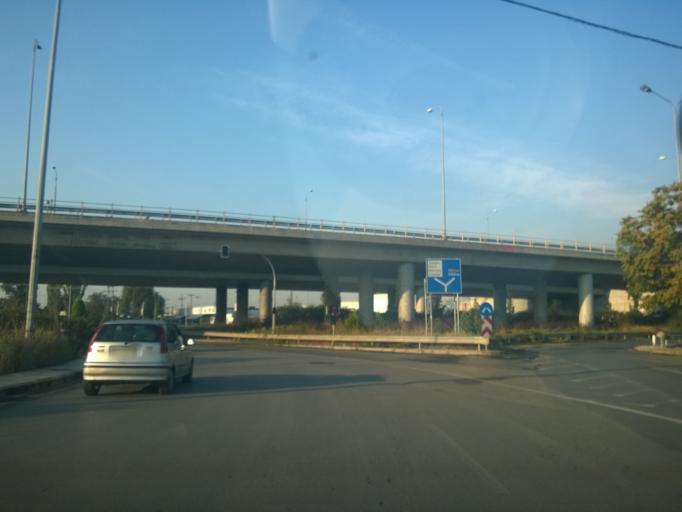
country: GR
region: Central Macedonia
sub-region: Nomos Thessalonikis
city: Menemeni
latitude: 40.6538
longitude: 22.8999
